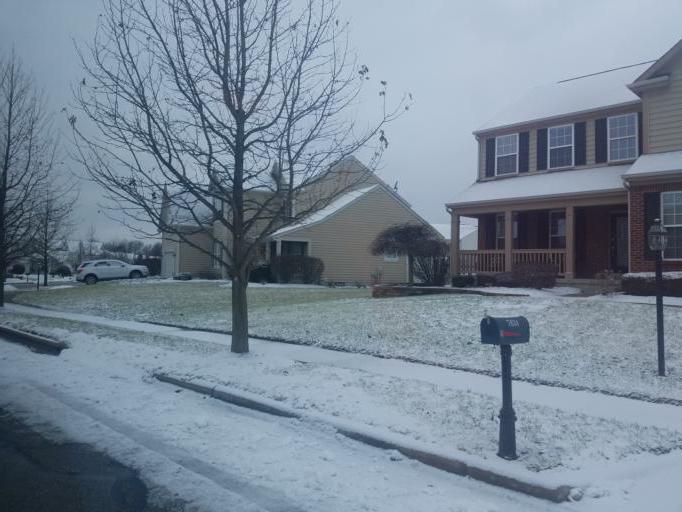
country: US
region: Ohio
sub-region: Franklin County
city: Reynoldsburg
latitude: 40.0153
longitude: -82.7914
